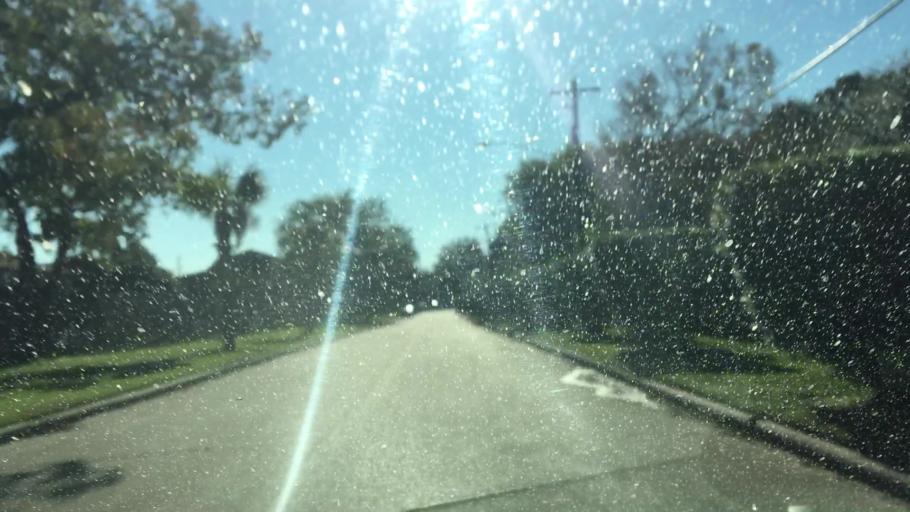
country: US
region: Texas
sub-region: Harris County
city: Nassau Bay
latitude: 29.5380
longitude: -95.0996
